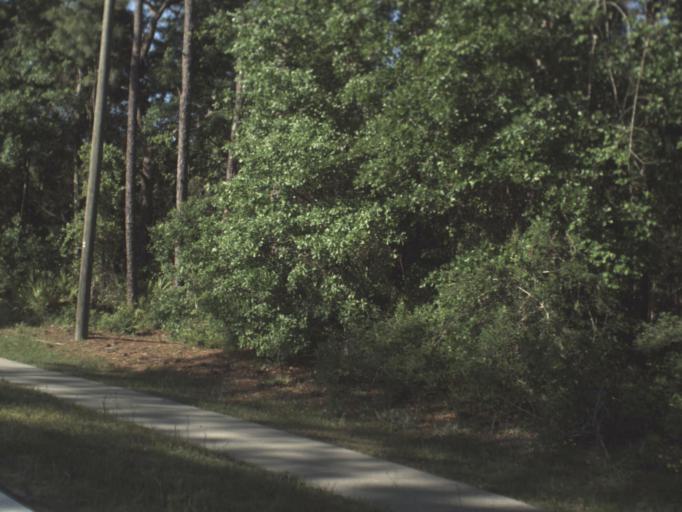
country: US
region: Florida
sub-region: Gulf County
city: Wewahitchka
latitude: 30.0230
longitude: -84.9800
